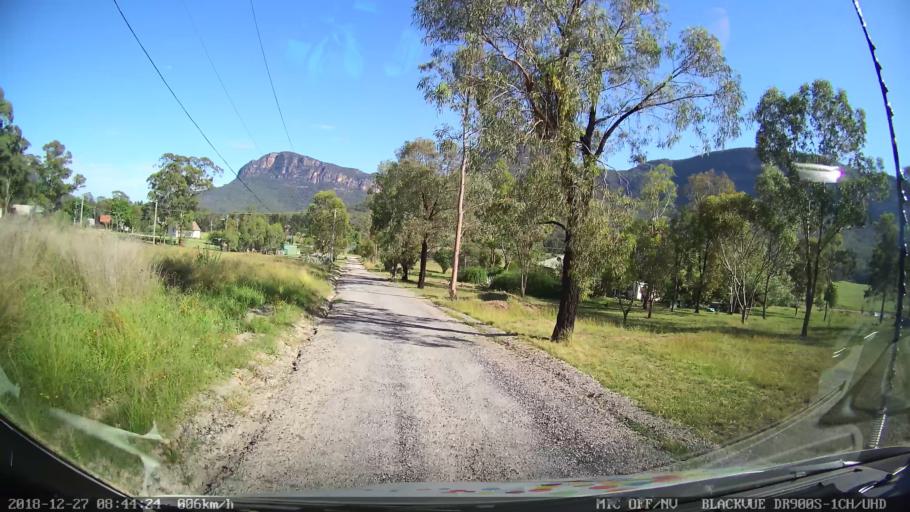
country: AU
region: New South Wales
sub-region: Lithgow
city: Portland
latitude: -33.1246
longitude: 150.2833
